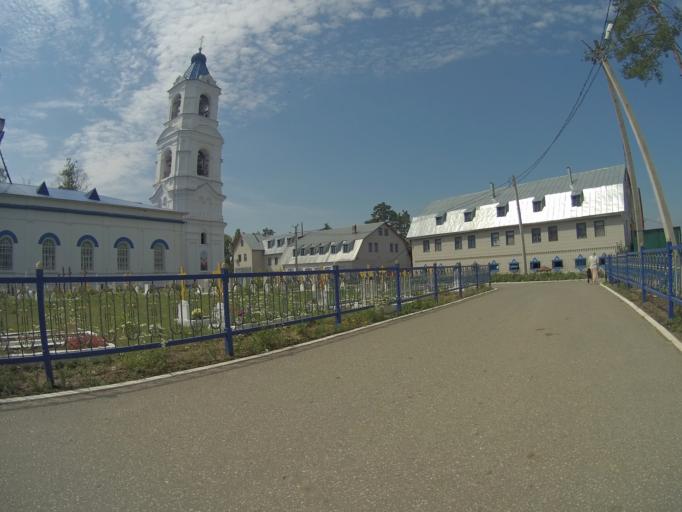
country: RU
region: Vladimir
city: Sudogda
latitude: 56.1483
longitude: 40.8189
